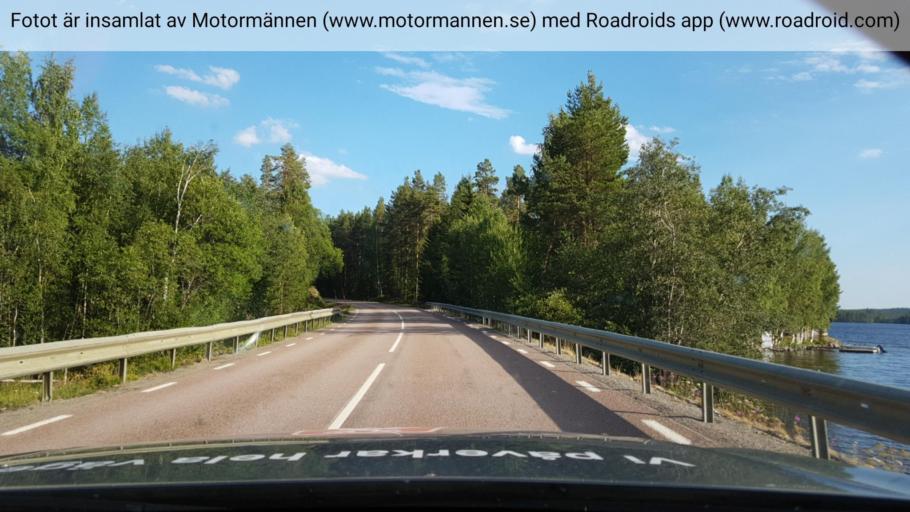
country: SE
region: Vaesternorrland
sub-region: Solleftea Kommun
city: As
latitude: 63.5924
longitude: 16.2810
